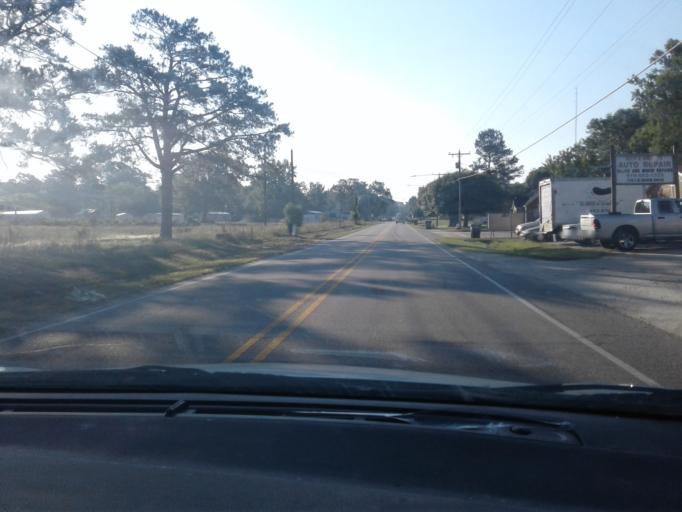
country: US
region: North Carolina
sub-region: Harnett County
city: Erwin
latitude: 35.3187
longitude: -78.6533
